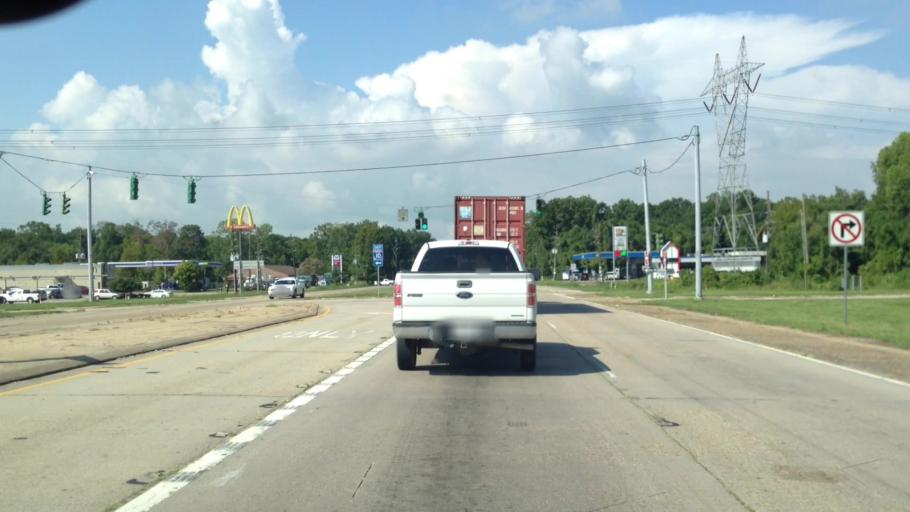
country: US
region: Louisiana
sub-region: Ascension Parish
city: Sorrento
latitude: 30.1715
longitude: -90.8771
